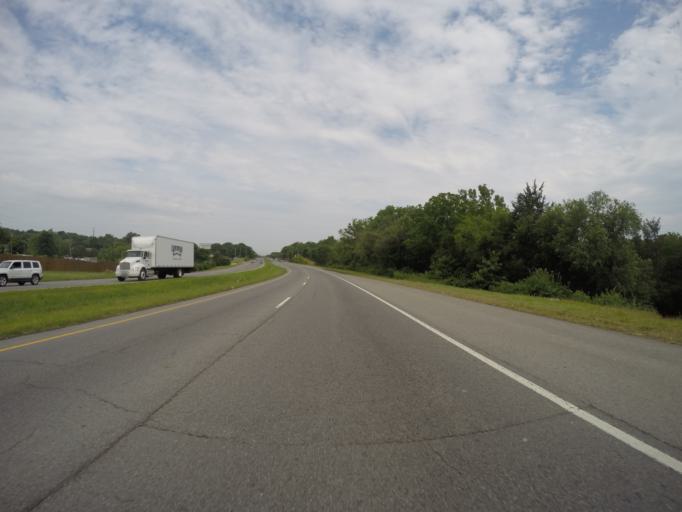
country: US
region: Tennessee
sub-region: Davidson County
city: Lakewood
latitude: 36.2633
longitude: -86.6820
